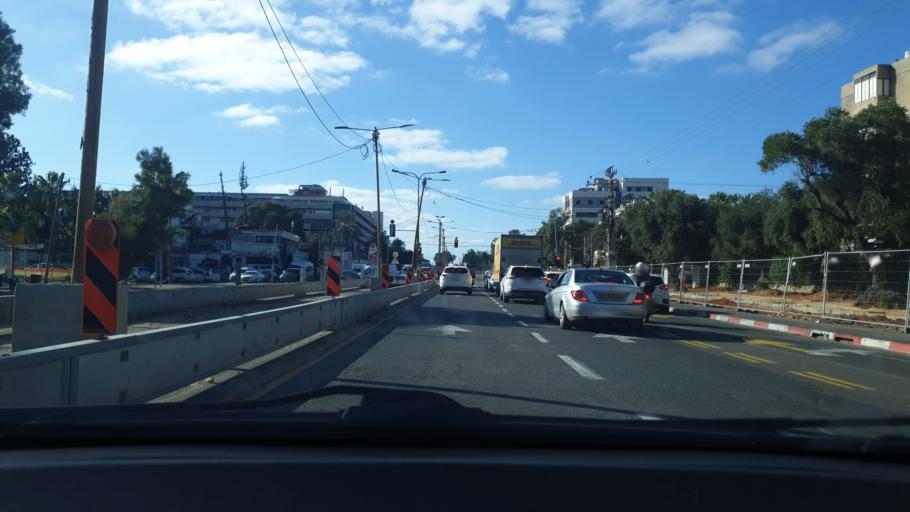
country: IL
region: Tel Aviv
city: Yafo
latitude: 32.0401
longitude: 34.7756
